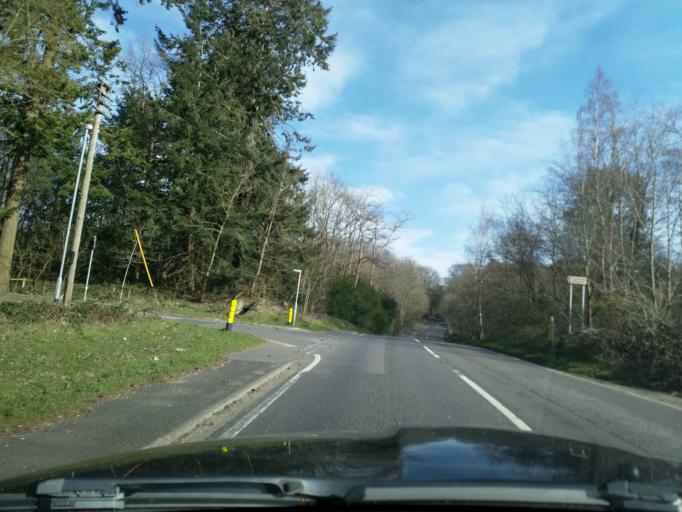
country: GB
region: England
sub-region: Hampshire
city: Aldershot
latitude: 51.2660
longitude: -0.7842
